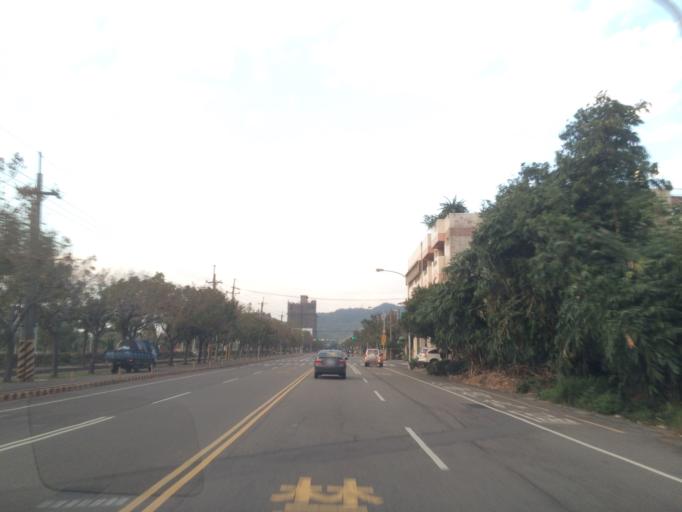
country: TW
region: Taiwan
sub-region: Taichung City
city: Taichung
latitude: 24.1647
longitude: 120.7334
